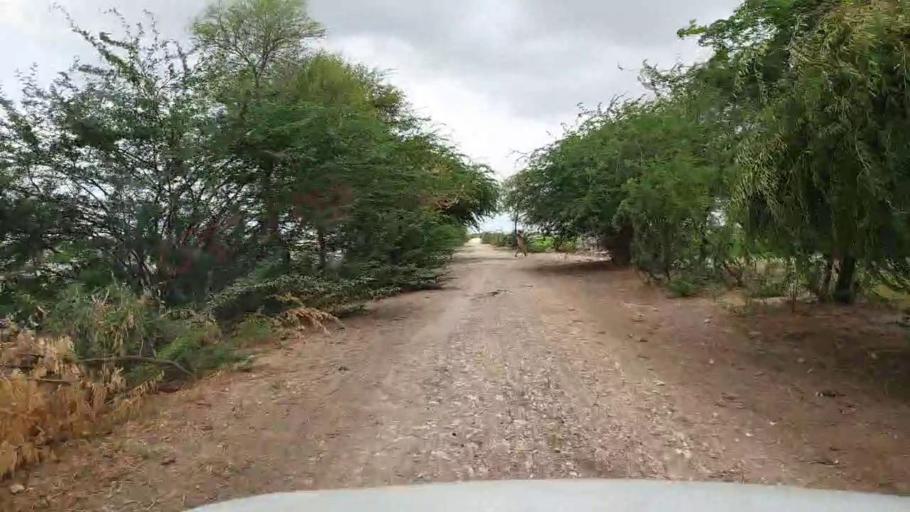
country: PK
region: Sindh
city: Kario
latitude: 24.7482
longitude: 68.4812
